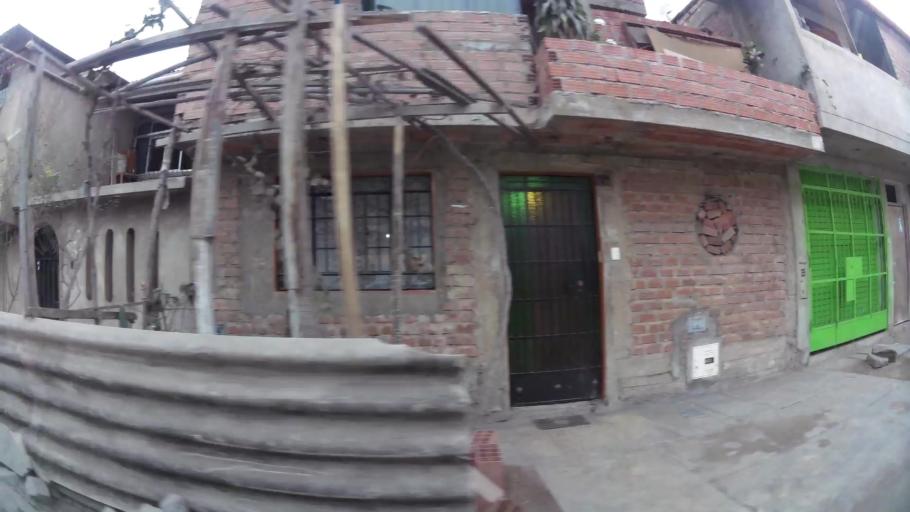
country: PE
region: Lima
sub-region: Lima
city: Surco
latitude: -12.1752
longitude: -76.9654
